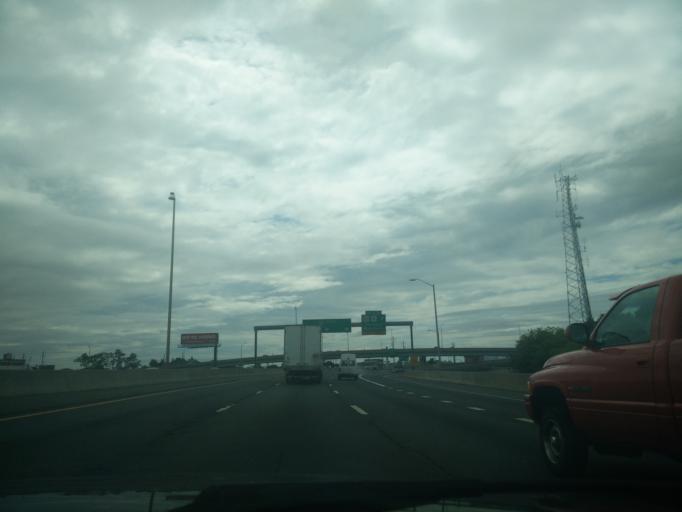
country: US
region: Connecticut
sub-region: Fairfield County
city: Bridgeport
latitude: 41.1725
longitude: -73.1901
